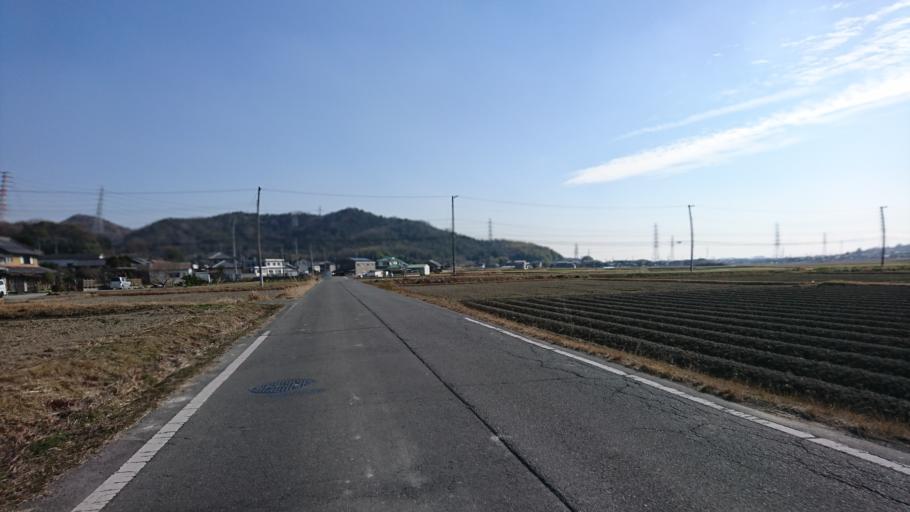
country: JP
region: Hyogo
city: Kakogawacho-honmachi
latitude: 34.8207
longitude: 134.8497
